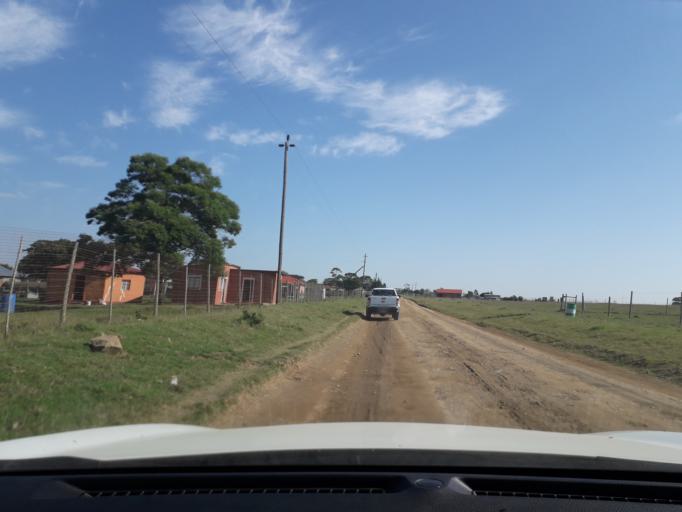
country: ZA
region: Eastern Cape
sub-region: Buffalo City Metropolitan Municipality
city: Bhisho
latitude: -32.9715
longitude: 27.3155
